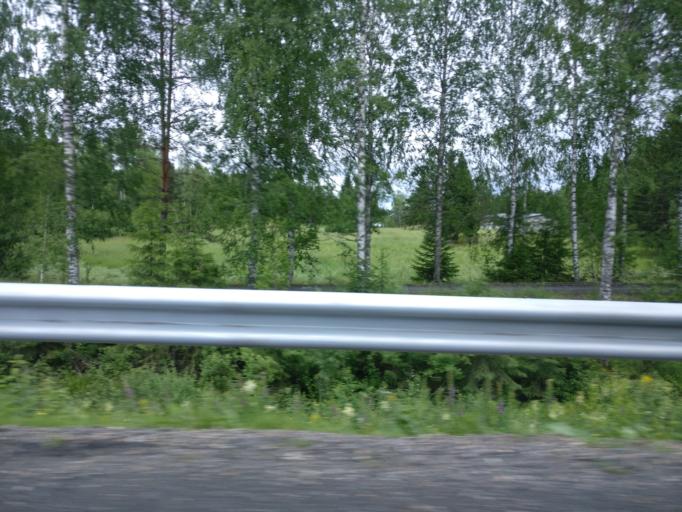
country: FI
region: Northern Savo
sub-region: Varkaus
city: Leppaevirta
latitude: 62.5975
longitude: 27.6081
